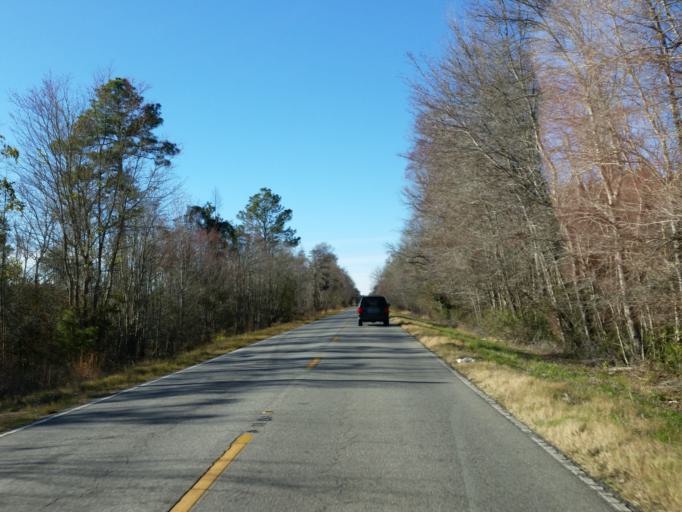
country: US
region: Georgia
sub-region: Echols County
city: Statenville
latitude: 30.6521
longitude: -83.1467
